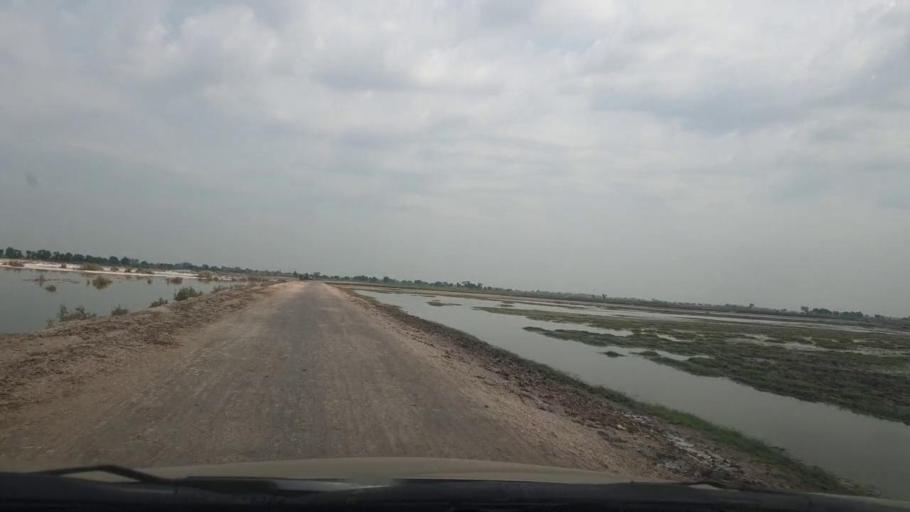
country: PK
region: Sindh
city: Ratodero
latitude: 27.7087
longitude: 68.2287
